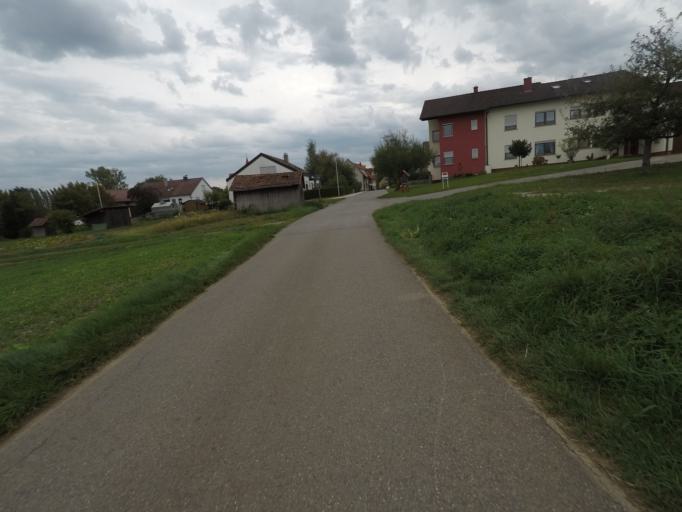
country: DE
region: Baden-Wuerttemberg
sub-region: Regierungsbezirk Stuttgart
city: Herrenberg
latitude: 48.5602
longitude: 8.9008
